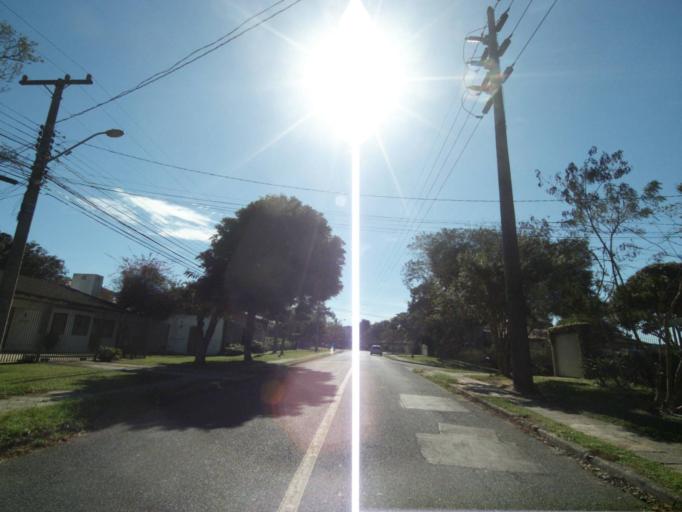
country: BR
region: Parana
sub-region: Curitiba
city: Curitiba
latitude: -25.4072
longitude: -49.2810
